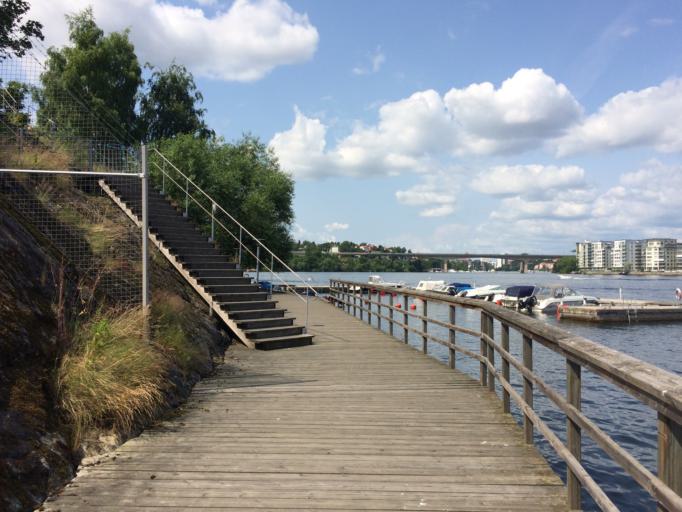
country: SE
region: Stockholm
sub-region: Solna Kommun
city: Solna
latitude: 59.3184
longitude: 18.0085
